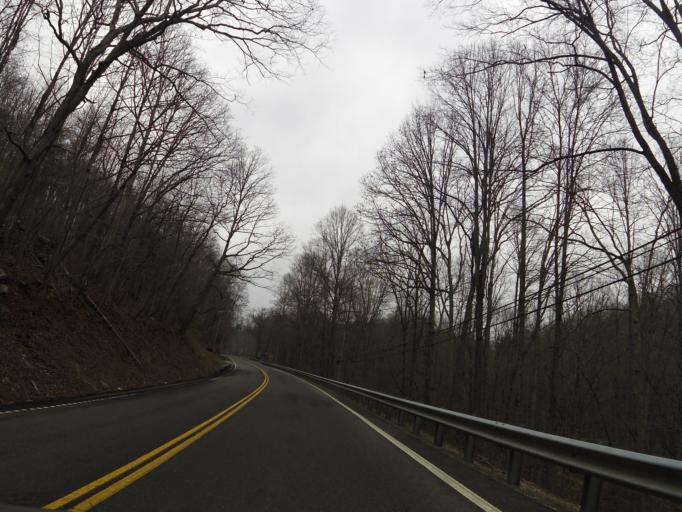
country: US
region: Tennessee
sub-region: Morgan County
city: Wartburg
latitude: 36.1549
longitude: -84.6439
